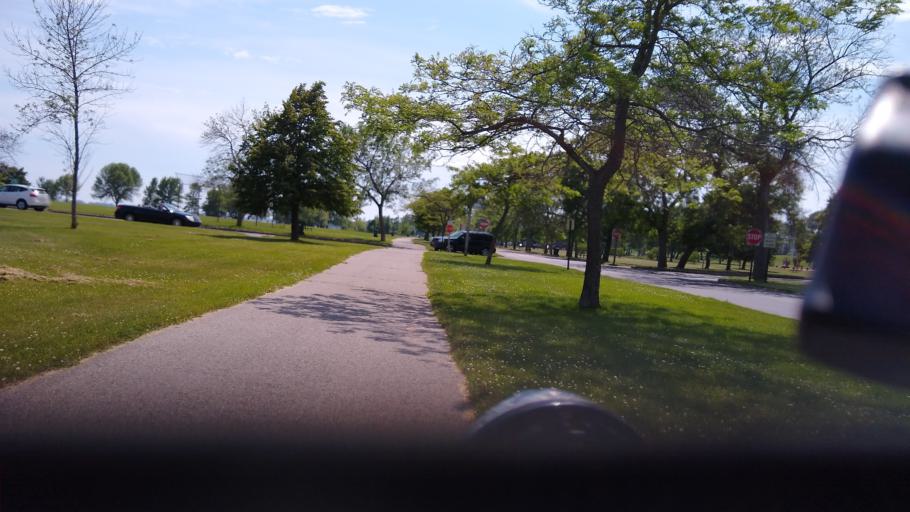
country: US
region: Michigan
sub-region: Delta County
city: Escanaba
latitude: 45.7417
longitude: -87.0498
